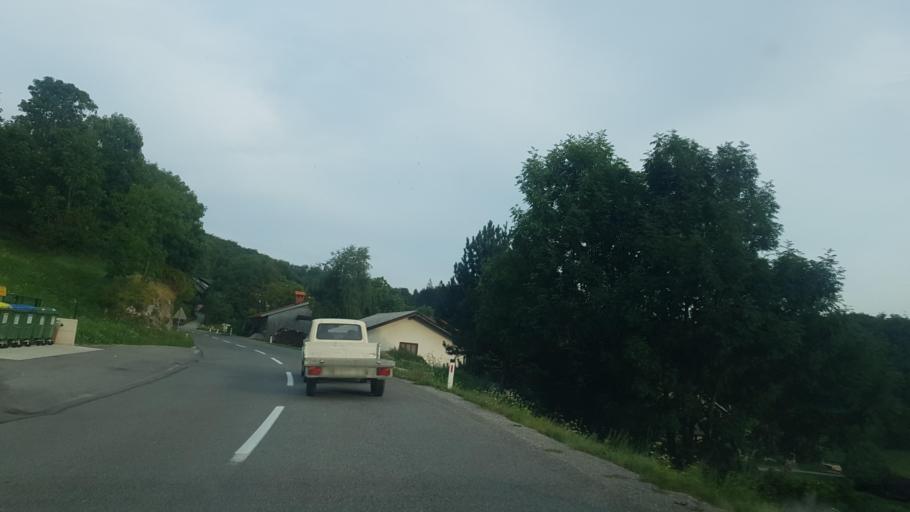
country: SI
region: Vipava
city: Vipava
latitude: 45.8645
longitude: 14.0612
